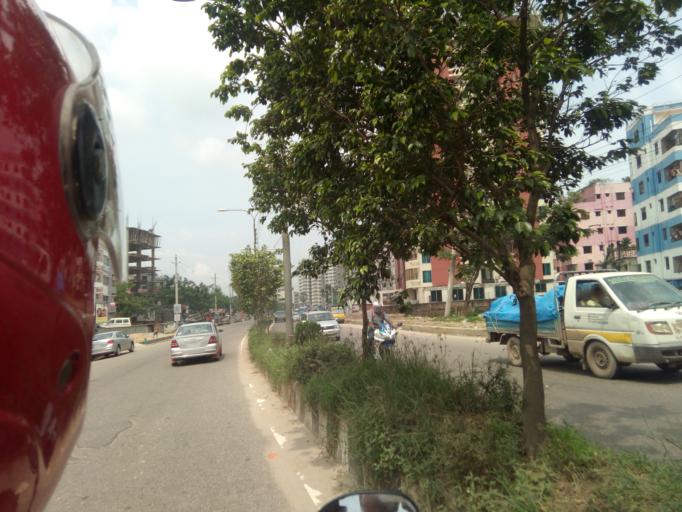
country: BD
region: Dhaka
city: Tungi
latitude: 23.8214
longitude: 90.3913
